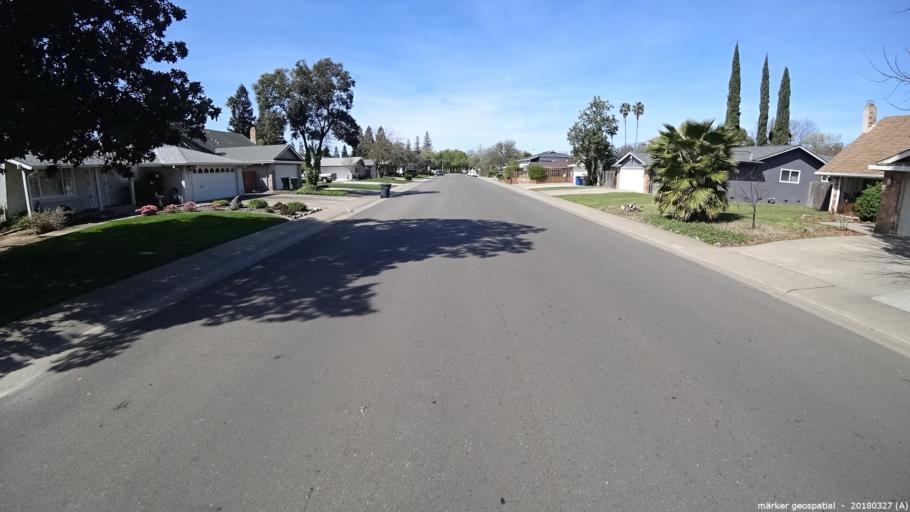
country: US
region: California
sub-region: Sacramento County
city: Rosemont
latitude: 38.5509
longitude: -121.3702
